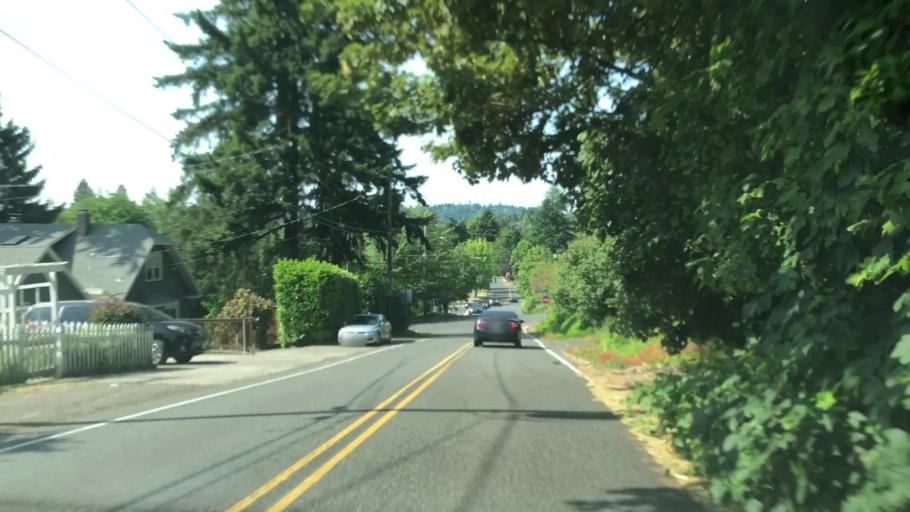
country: US
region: Oregon
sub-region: Washington County
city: Garden Home-Whitford
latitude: 45.4660
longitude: -122.7180
